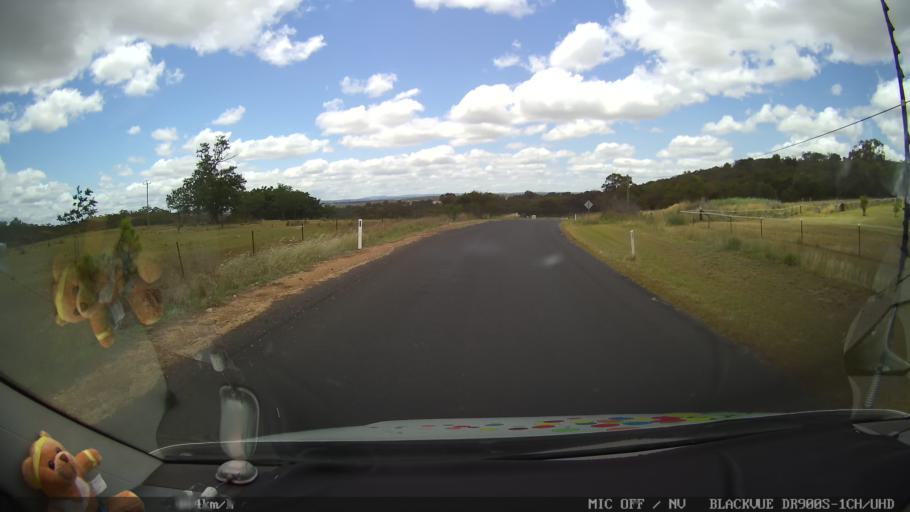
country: AU
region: New South Wales
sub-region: Glen Innes Severn
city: Glen Innes
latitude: -29.4287
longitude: 151.6483
